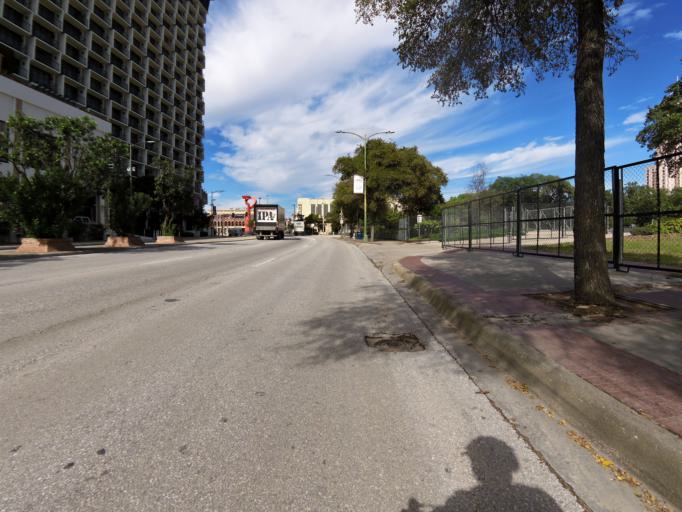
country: US
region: Texas
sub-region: Bexar County
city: San Antonio
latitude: 29.4218
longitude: -98.4876
